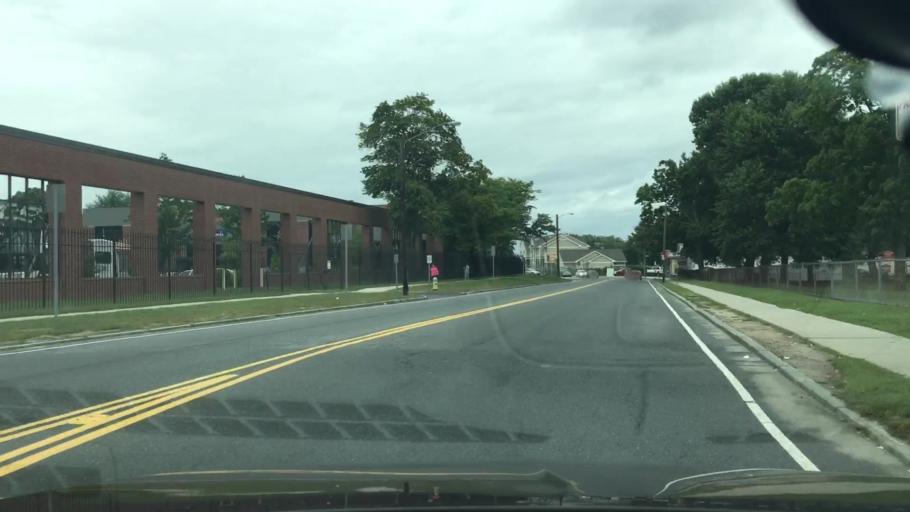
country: US
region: Massachusetts
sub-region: Hampden County
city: Springfield
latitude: 42.1102
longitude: -72.5747
